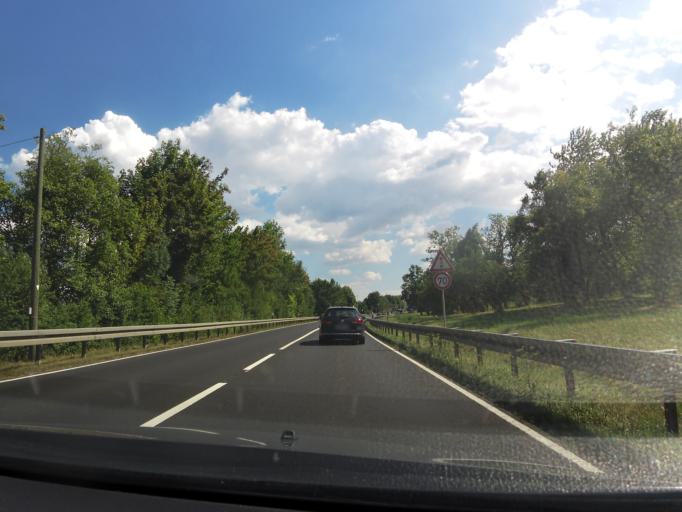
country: DE
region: Bavaria
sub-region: Regierungsbezirk Unterfranken
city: Margetshochheim
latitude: 49.8448
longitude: 9.8589
